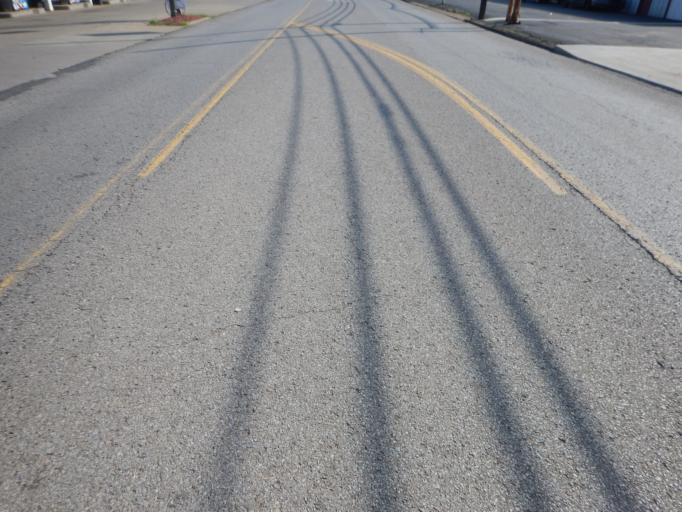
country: US
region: Ohio
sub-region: Muskingum County
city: South Zanesville
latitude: 39.9185
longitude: -82.0113
